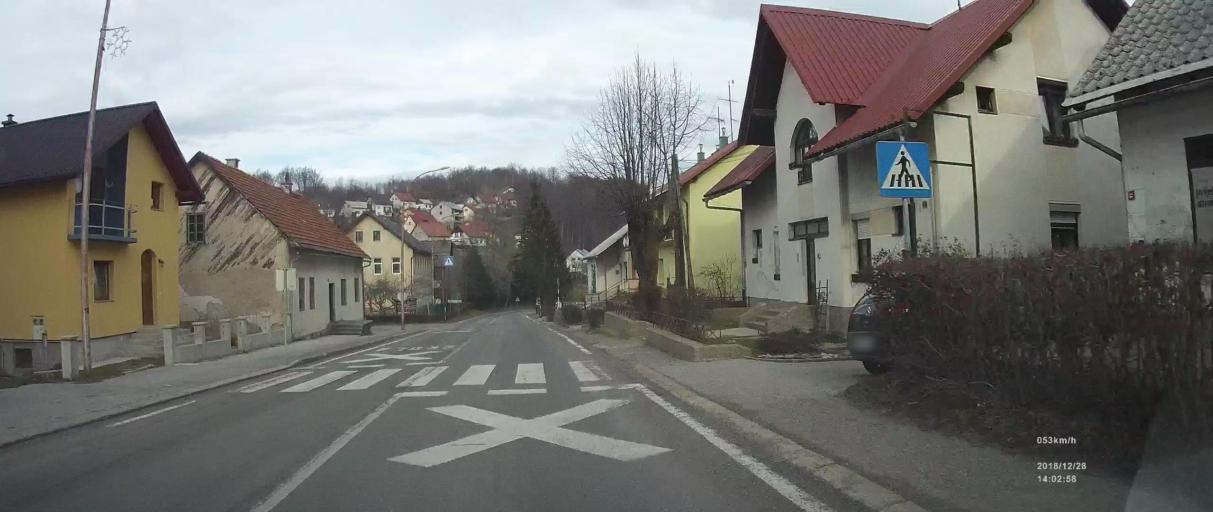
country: SI
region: Kostel
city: Kostel
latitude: 45.4329
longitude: 14.9054
